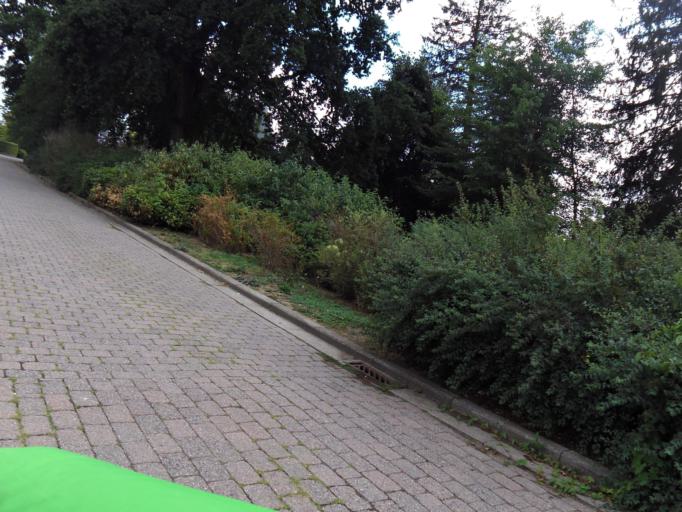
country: BE
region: Wallonia
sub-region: Province de Namur
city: Bievre
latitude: 49.9387
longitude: 5.0213
